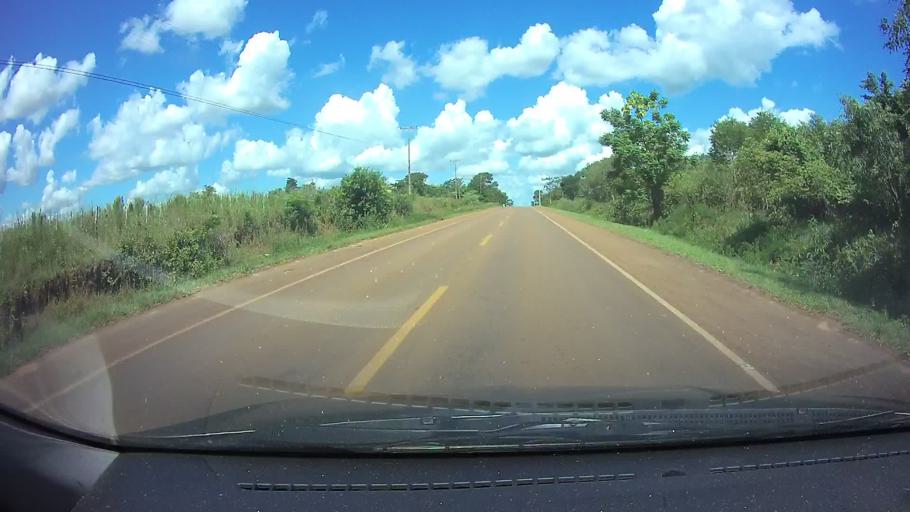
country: PY
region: Paraguari
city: La Colmena
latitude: -25.8997
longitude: -56.7847
